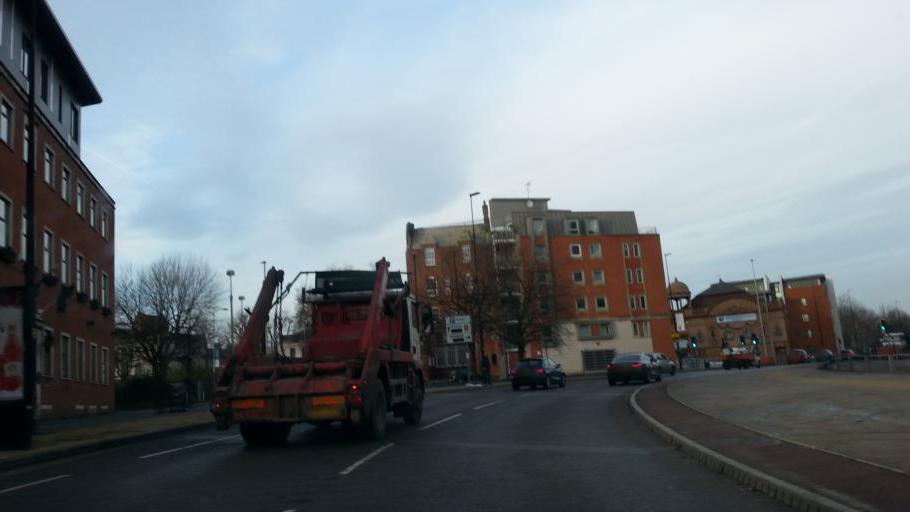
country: GB
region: England
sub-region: Manchester
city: Hulme
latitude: 53.4824
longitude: -2.2577
